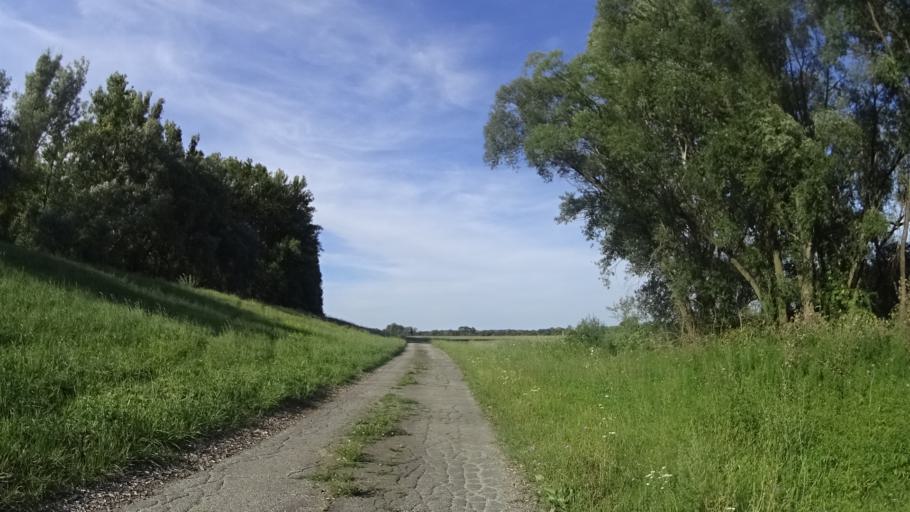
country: AT
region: Lower Austria
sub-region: Politischer Bezirk Ganserndorf
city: Drosing
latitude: 48.5242
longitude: 16.9542
